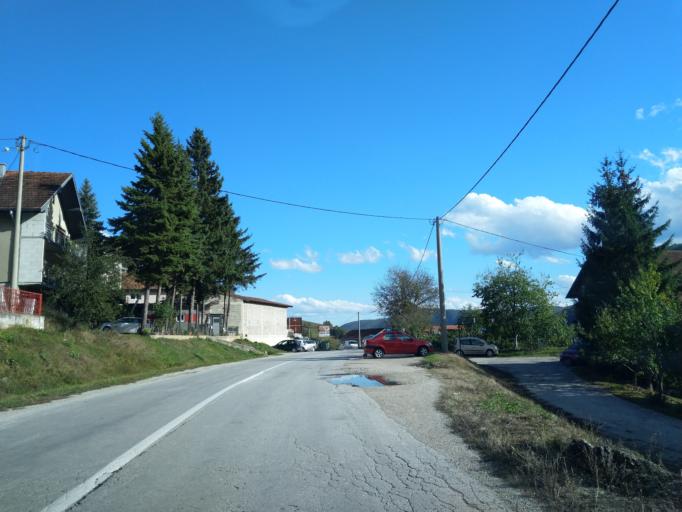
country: RS
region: Central Serbia
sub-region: Zlatiborski Okrug
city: Uzice
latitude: 43.8704
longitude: 19.7965
